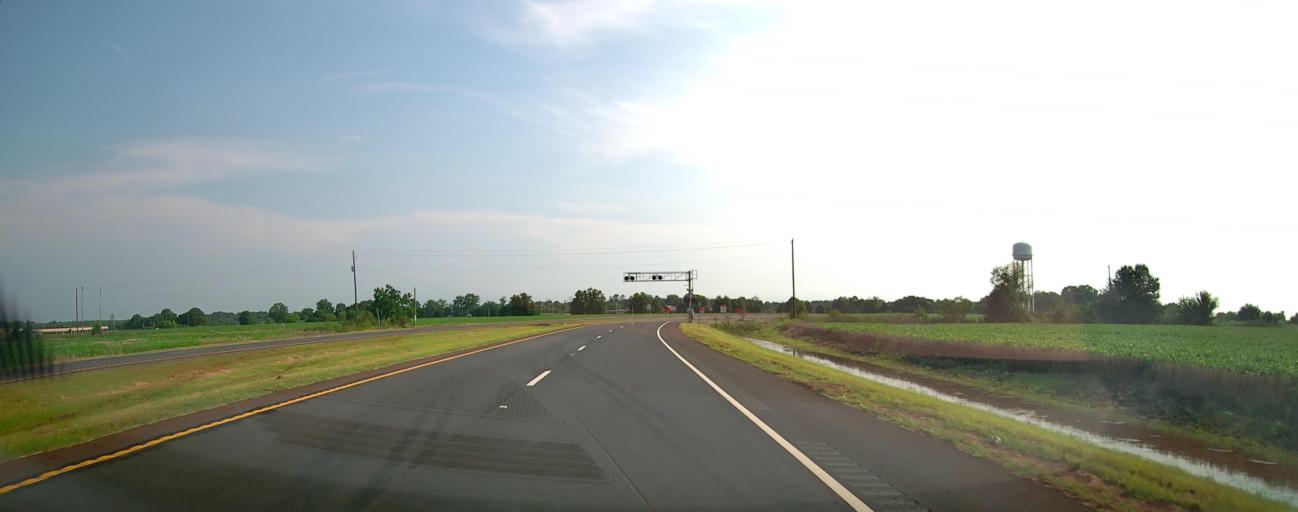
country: US
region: Georgia
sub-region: Peach County
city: Fort Valley
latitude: 32.5739
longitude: -83.9114
